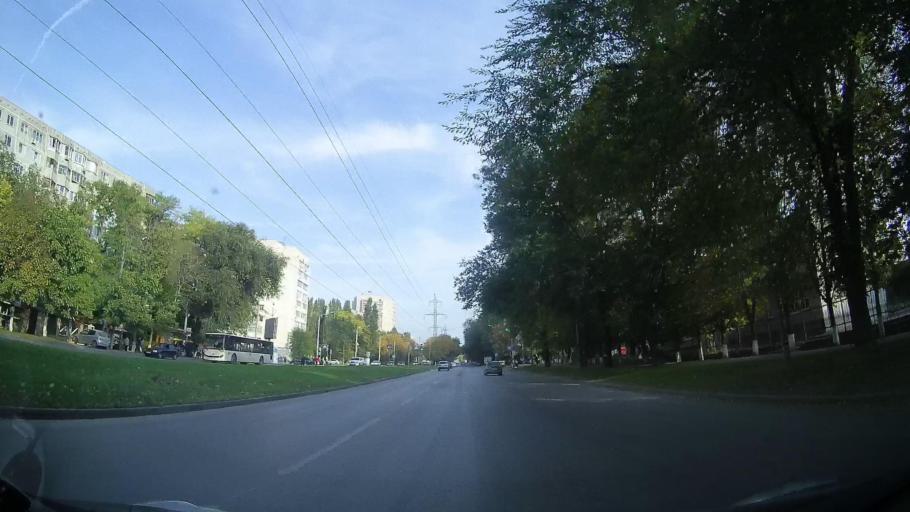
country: RU
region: Rostov
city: Imeni Chkalova
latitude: 47.2816
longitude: 39.7613
